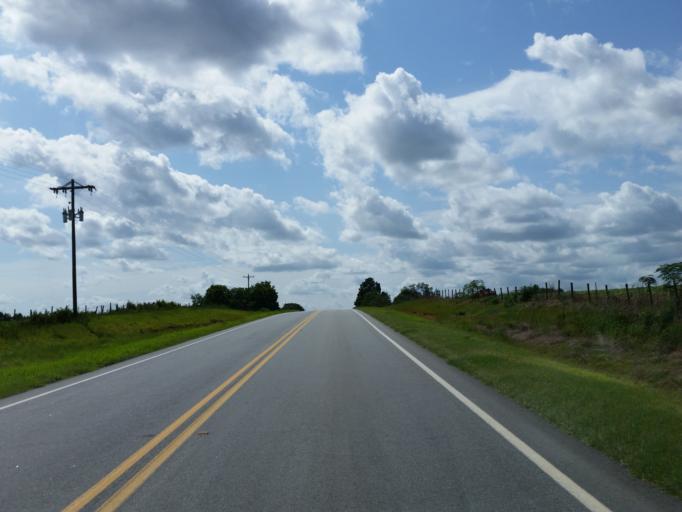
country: US
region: Georgia
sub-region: Turner County
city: Ashburn
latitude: 31.6356
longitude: -83.5154
